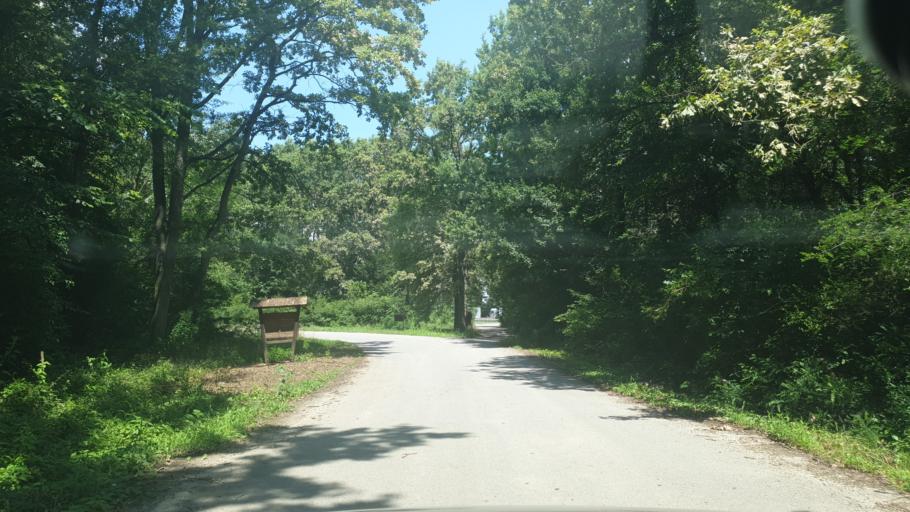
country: RS
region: Autonomna Pokrajina Vojvodina
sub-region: Sremski Okrug
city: Sid
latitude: 45.0422
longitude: 19.1383
